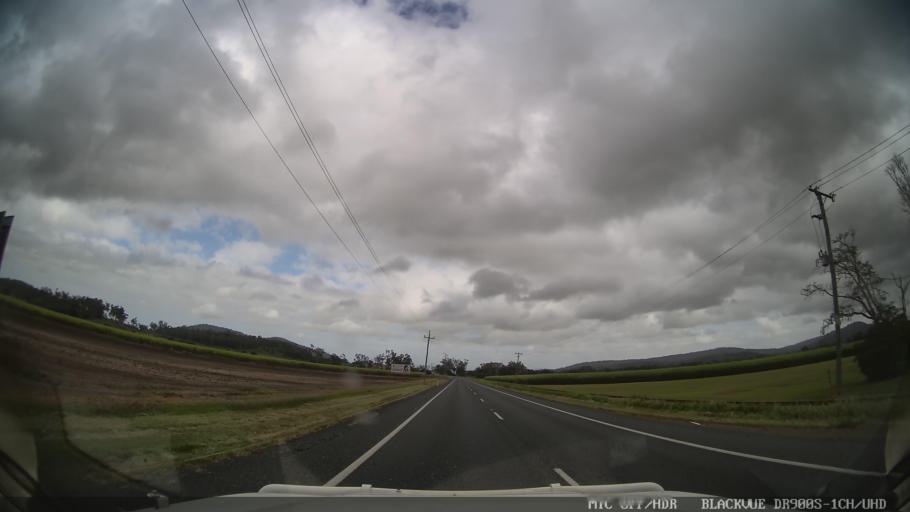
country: AU
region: Queensland
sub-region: Whitsunday
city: Proserpine
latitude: -20.3459
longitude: 148.6280
